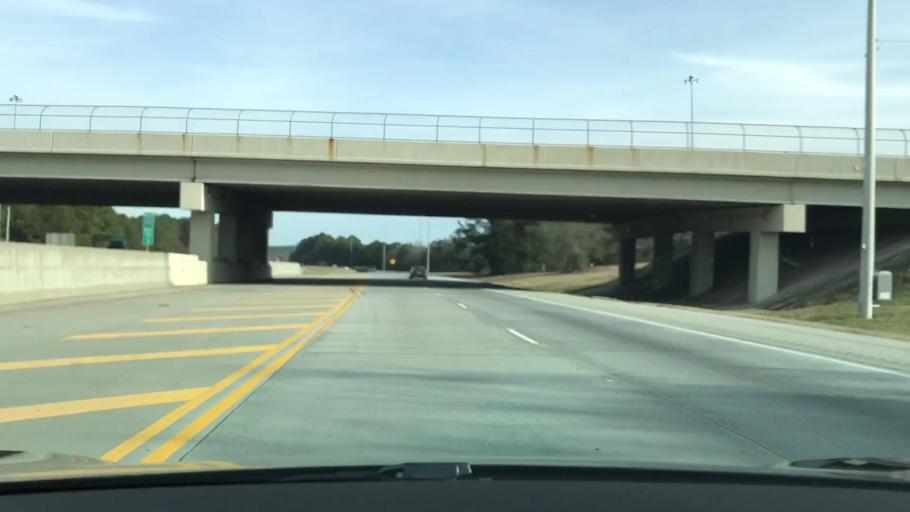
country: US
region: Georgia
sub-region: Newton County
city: Covington
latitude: 33.6127
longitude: -83.8256
